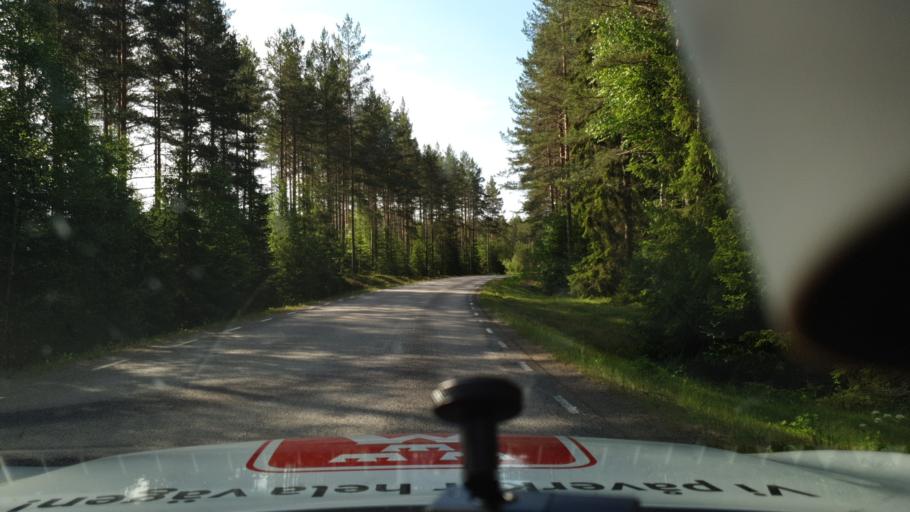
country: SE
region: Vaermland
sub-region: Torsby Kommun
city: Torsby
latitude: 59.9619
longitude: 12.9092
